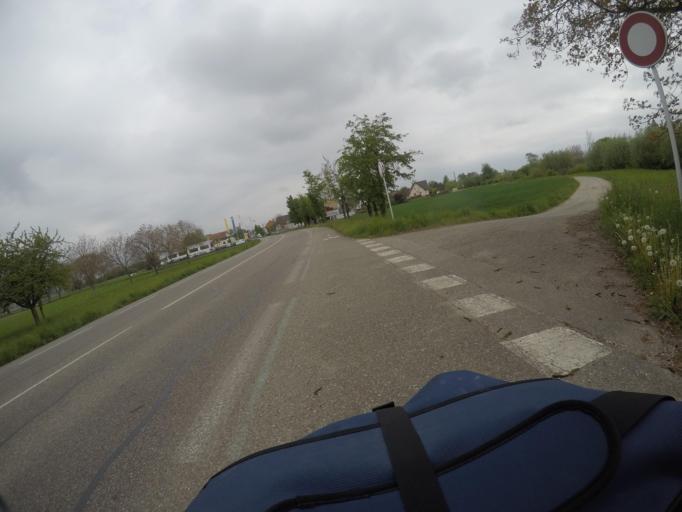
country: FR
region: Alsace
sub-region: Departement du Bas-Rhin
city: Kilstett
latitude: 48.6849
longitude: 7.8682
